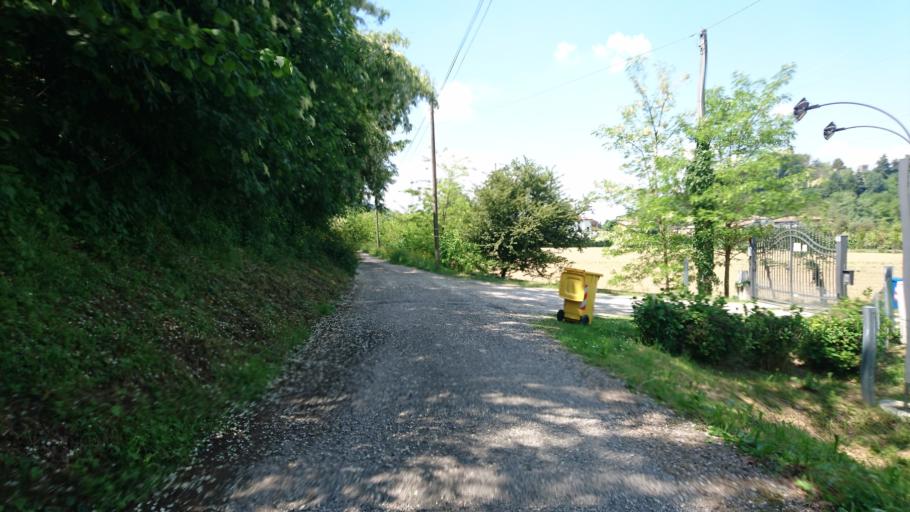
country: IT
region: Veneto
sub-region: Provincia di Padova
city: Treponti
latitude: 45.3714
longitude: 11.7089
